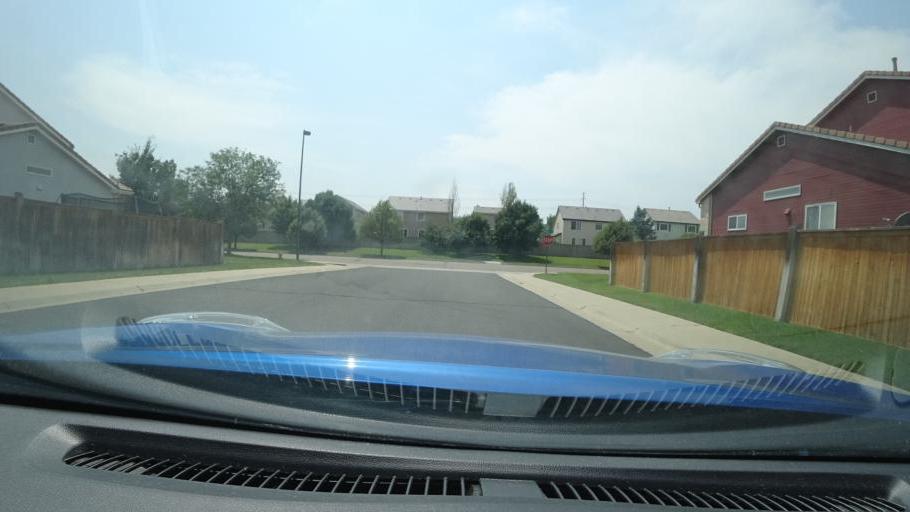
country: US
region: Colorado
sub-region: Adams County
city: Aurora
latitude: 39.7706
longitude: -104.7588
